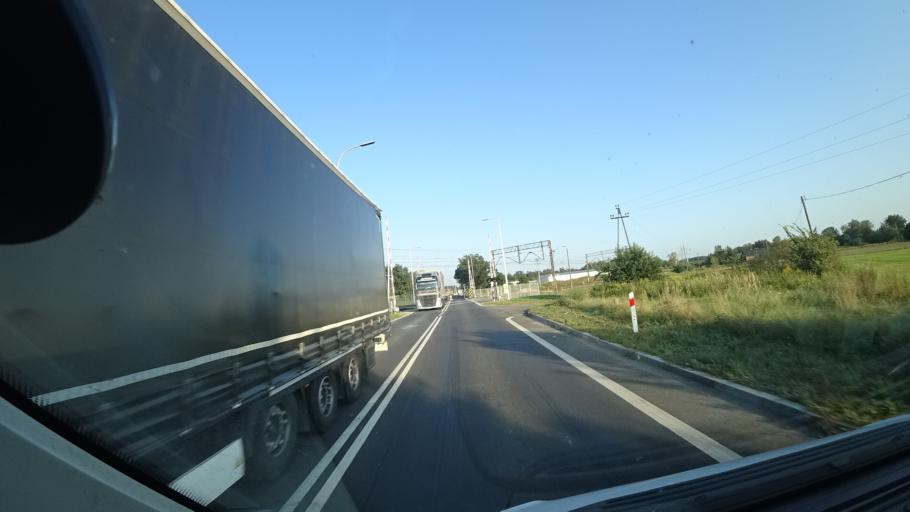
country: PL
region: Opole Voivodeship
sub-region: Powiat kedzierzynsko-kozielski
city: Bierawa
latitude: 50.2915
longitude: 18.2583
